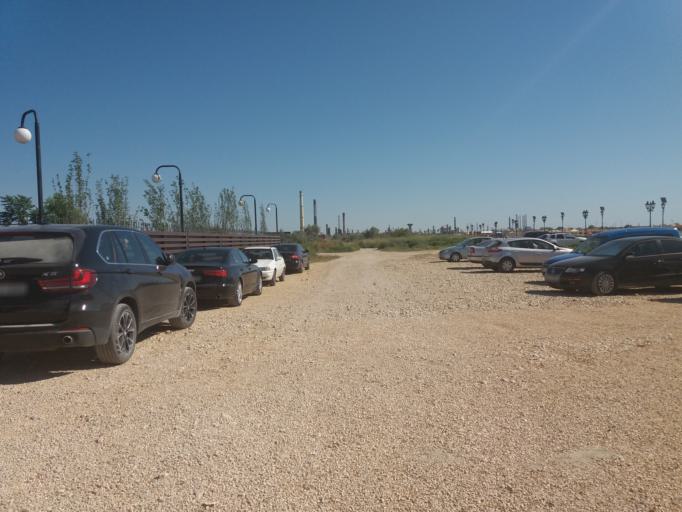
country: RO
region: Constanta
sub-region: Comuna Navodari
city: Navodari
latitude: 44.3208
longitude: 28.6355
